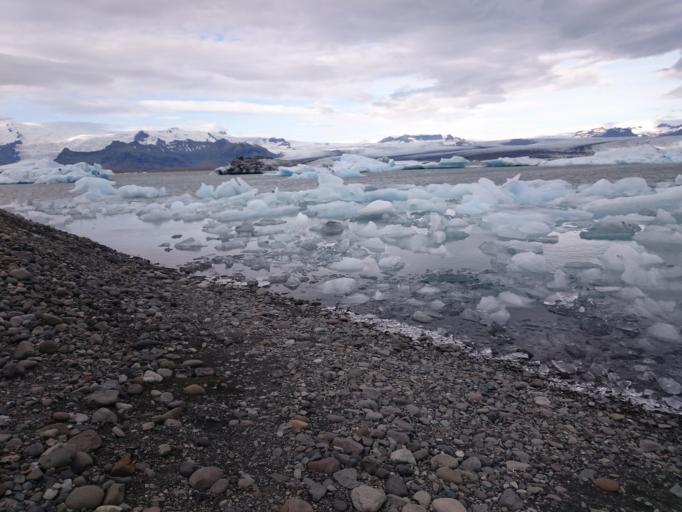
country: IS
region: East
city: Hoefn
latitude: 64.0529
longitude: -16.1781
